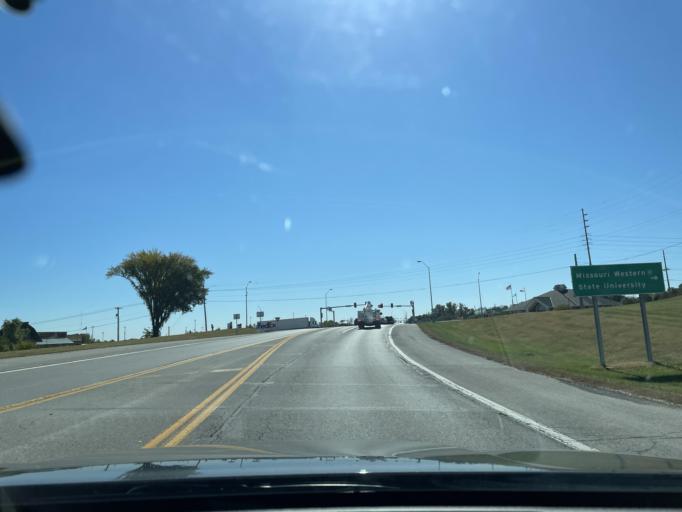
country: US
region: Missouri
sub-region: Buchanan County
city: Saint Joseph
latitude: 39.7568
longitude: -94.7682
